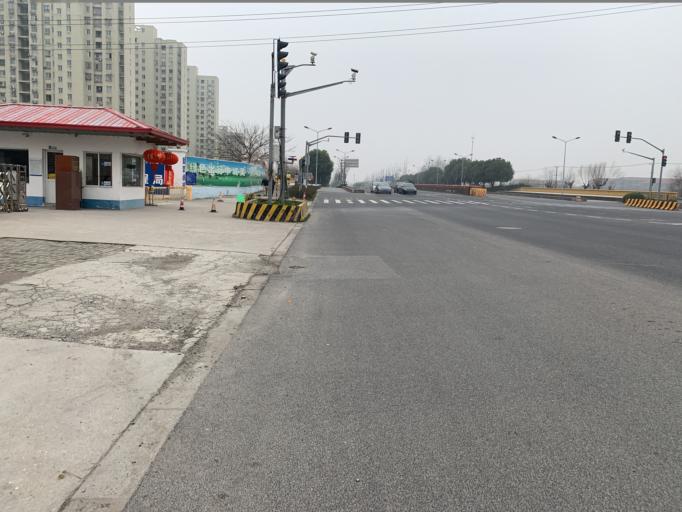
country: CN
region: Shanghai Shi
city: Huamu
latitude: 31.2445
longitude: 121.6212
